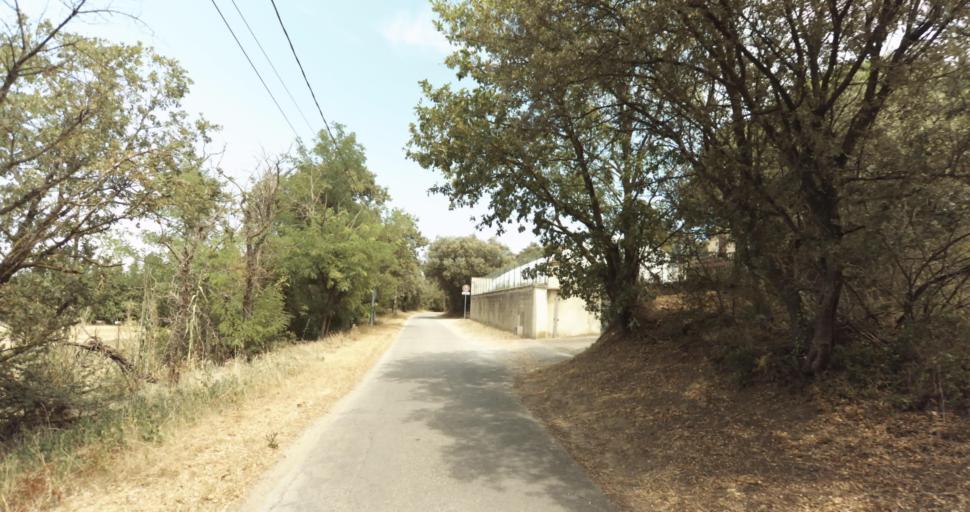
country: FR
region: Provence-Alpes-Cote d'Azur
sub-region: Departement du Vaucluse
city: Monteux
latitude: 44.0554
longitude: 4.9859
